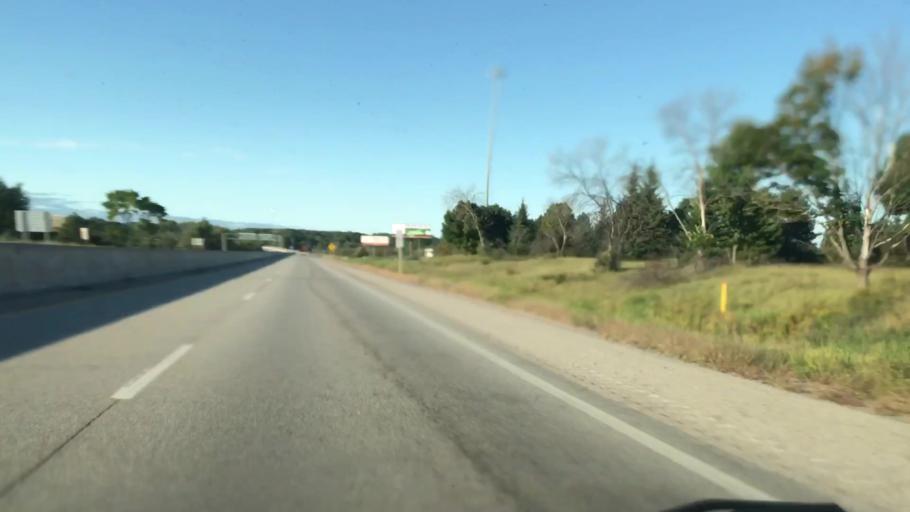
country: US
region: Michigan
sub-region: Chippewa County
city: Sault Ste. Marie
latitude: 46.4915
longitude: -84.3714
